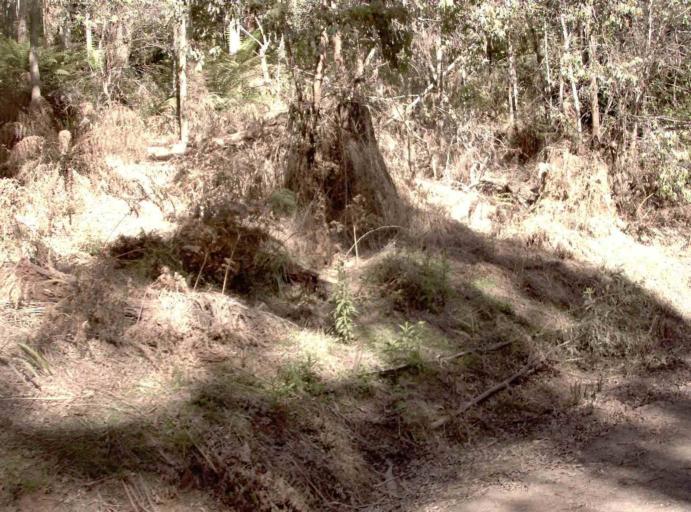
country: AU
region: New South Wales
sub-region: Bombala
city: Bombala
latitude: -37.2309
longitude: 148.7529
